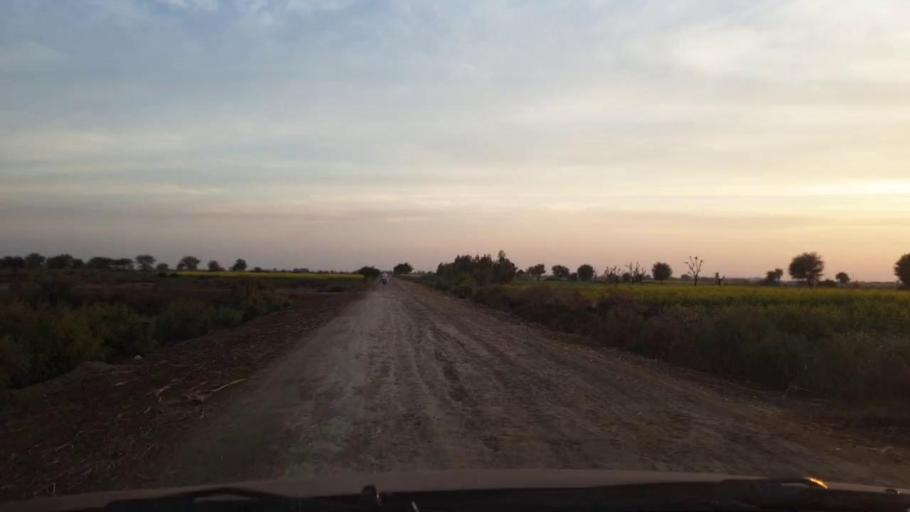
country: PK
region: Sindh
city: Sinjhoro
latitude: 26.0965
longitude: 68.7970
